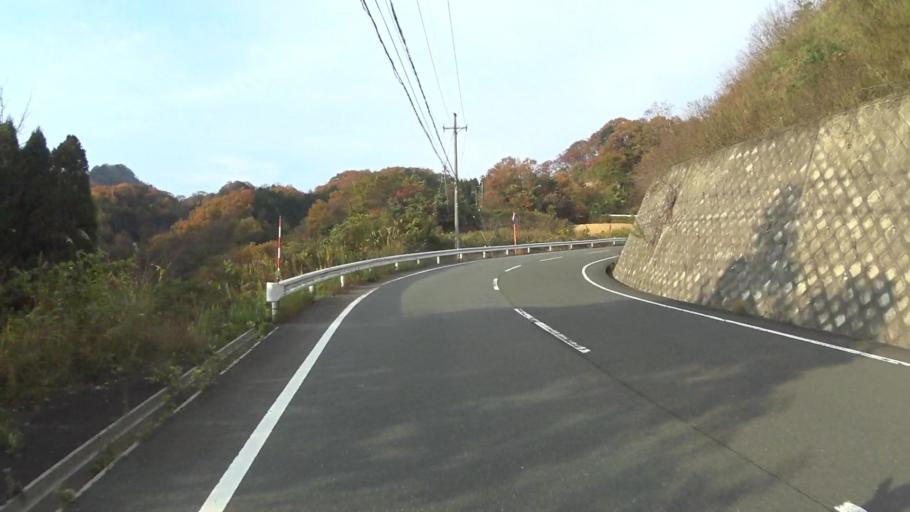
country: JP
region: Kyoto
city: Maizuru
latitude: 35.5137
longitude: 135.4574
